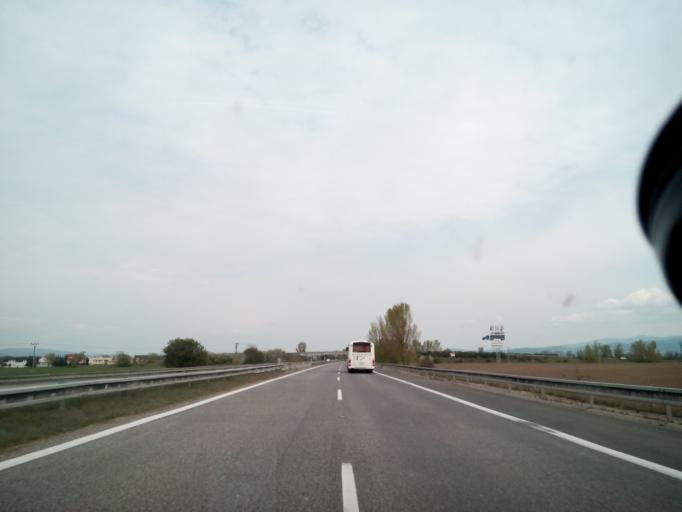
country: SK
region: Trnavsky
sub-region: Okres Trnava
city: Piestany
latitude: 48.6094
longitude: 17.7966
